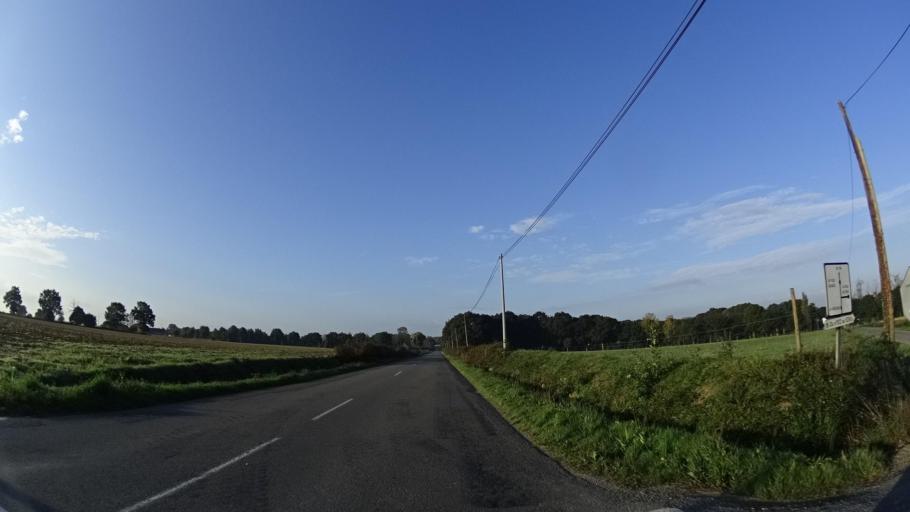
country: FR
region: Brittany
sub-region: Departement d'Ille-et-Vilaine
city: Quedillac
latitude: 48.2398
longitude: -2.1551
